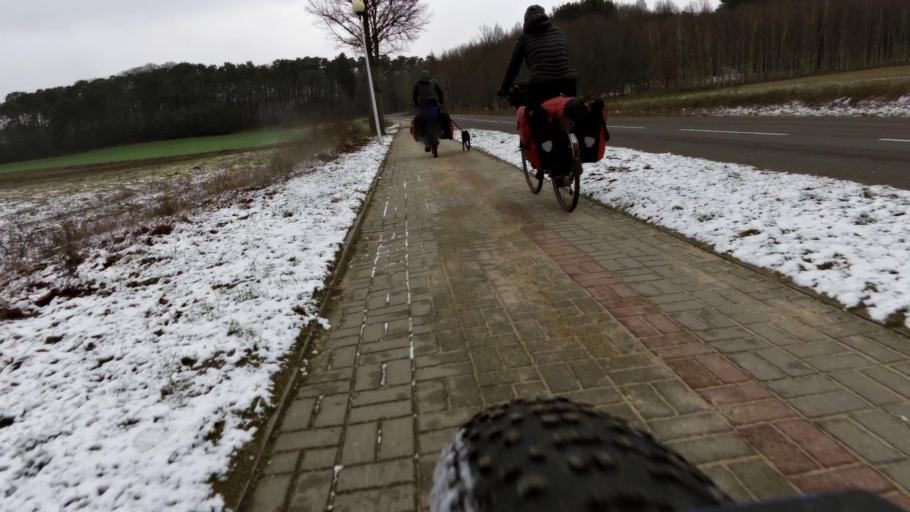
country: PL
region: West Pomeranian Voivodeship
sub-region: Powiat walecki
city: Miroslawiec
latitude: 53.3544
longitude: 16.0856
